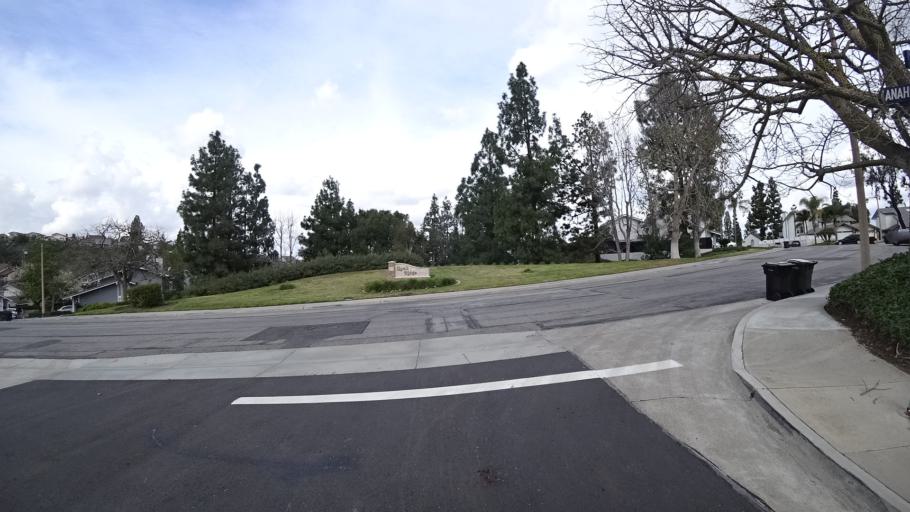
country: US
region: California
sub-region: Orange County
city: Villa Park
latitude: 33.8409
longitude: -117.7802
